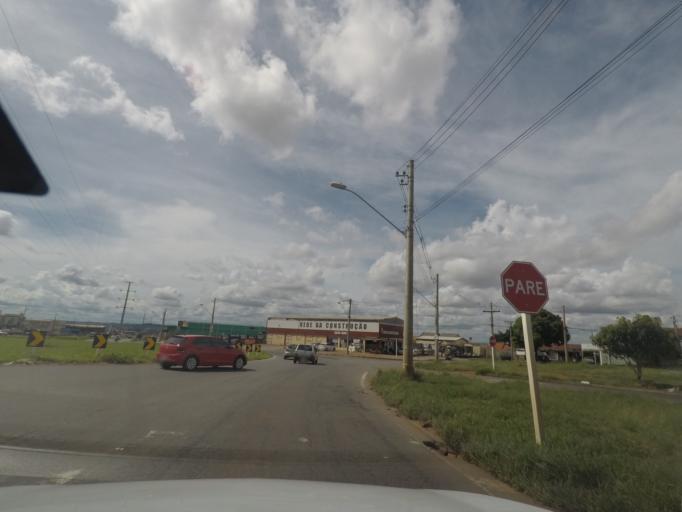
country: BR
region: Goias
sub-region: Goiania
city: Goiania
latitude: -16.7346
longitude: -49.3477
